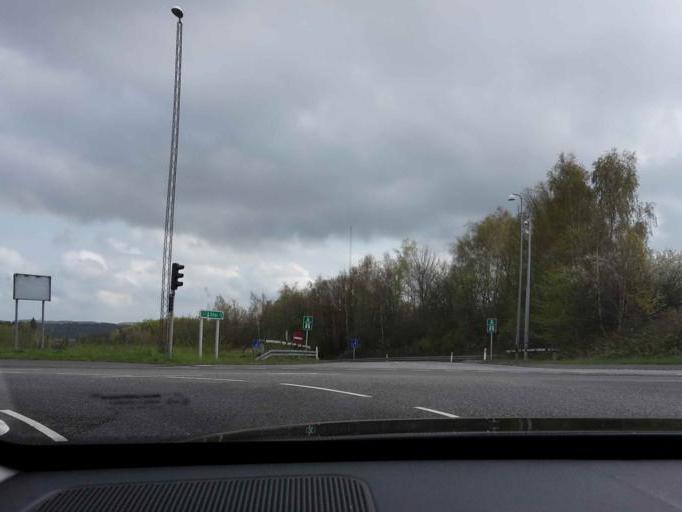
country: DK
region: South Denmark
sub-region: Vejle Kommune
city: Vejle
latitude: 55.6826
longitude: 9.5650
